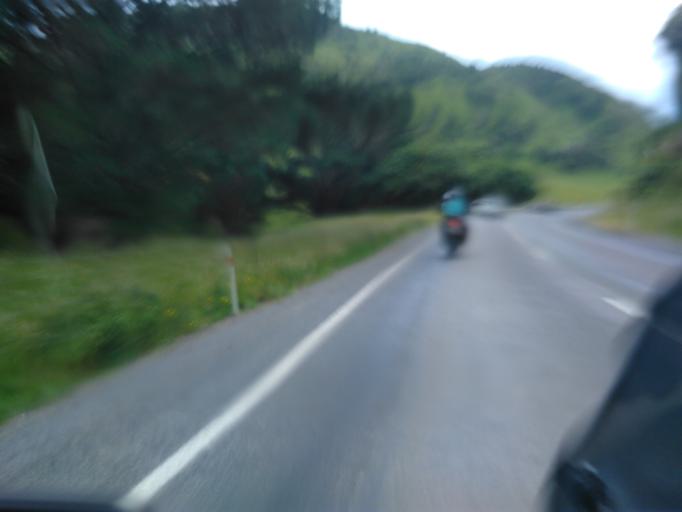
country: NZ
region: Bay of Plenty
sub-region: Opotiki District
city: Opotiki
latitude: -38.3782
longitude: 177.4793
